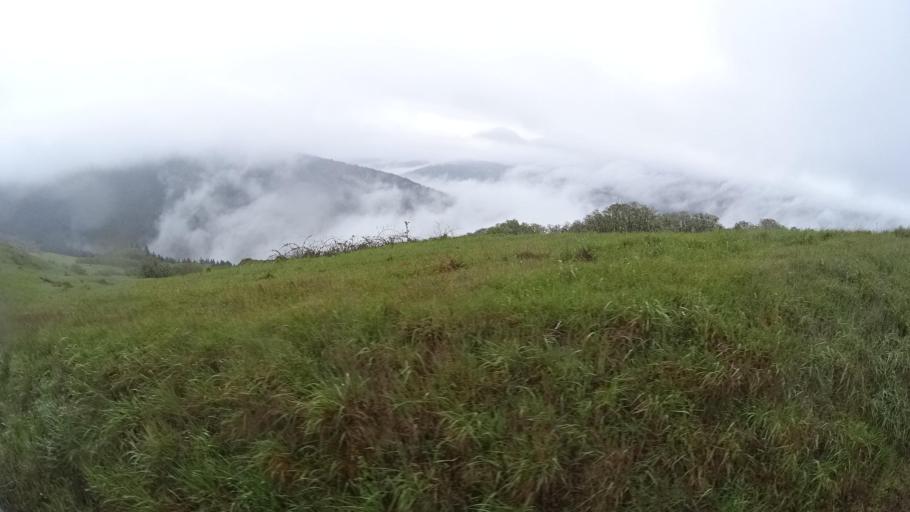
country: US
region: California
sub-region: Humboldt County
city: Westhaven-Moonstone
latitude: 41.1654
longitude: -123.9113
